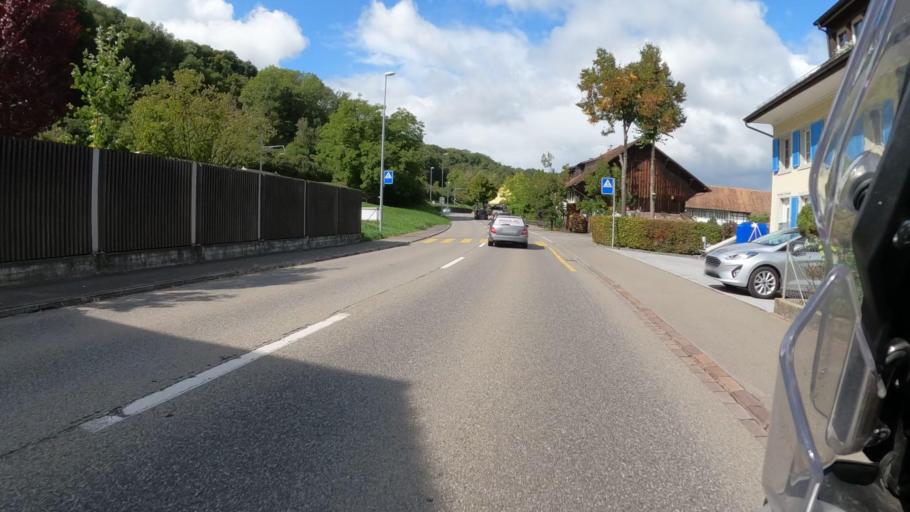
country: CH
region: Aargau
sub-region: Bezirk Zurzach
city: Bad Zurzach
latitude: 47.6010
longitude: 8.2779
